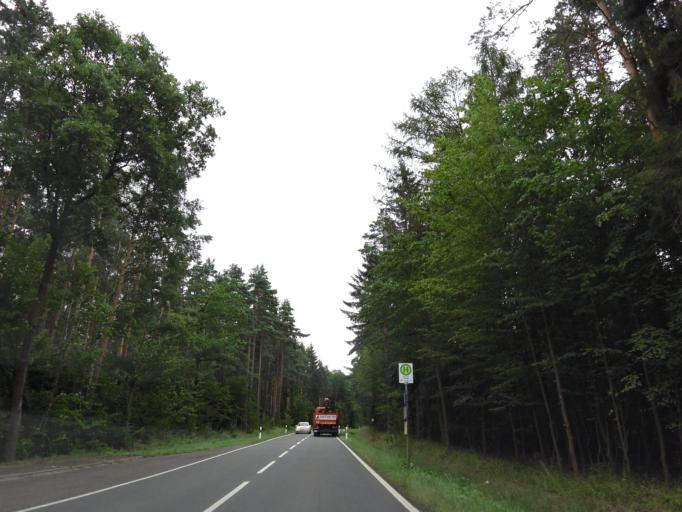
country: DE
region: Thuringia
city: Hainspitz
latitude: 50.9411
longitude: 11.8525
